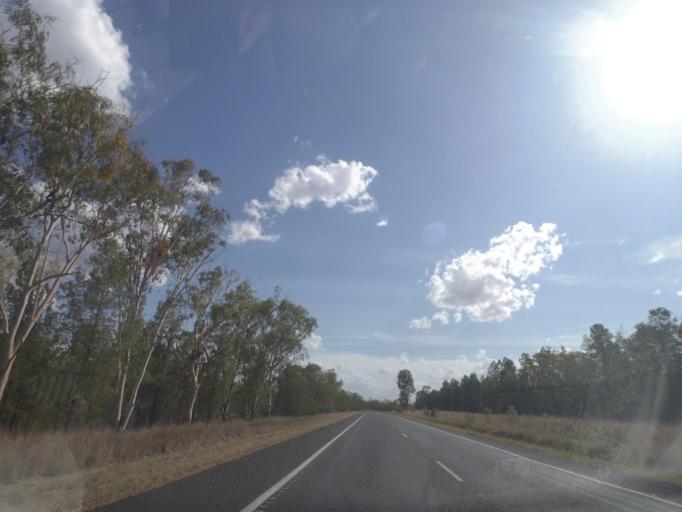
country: AU
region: New South Wales
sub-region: Moree Plains
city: Boggabilla
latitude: -28.5404
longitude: 150.8863
